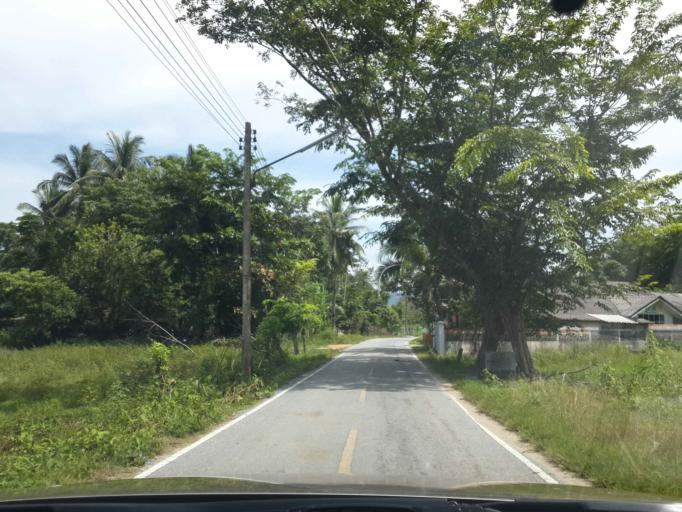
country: TH
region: Narathiwat
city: Rueso
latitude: 6.3983
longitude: 101.5152
